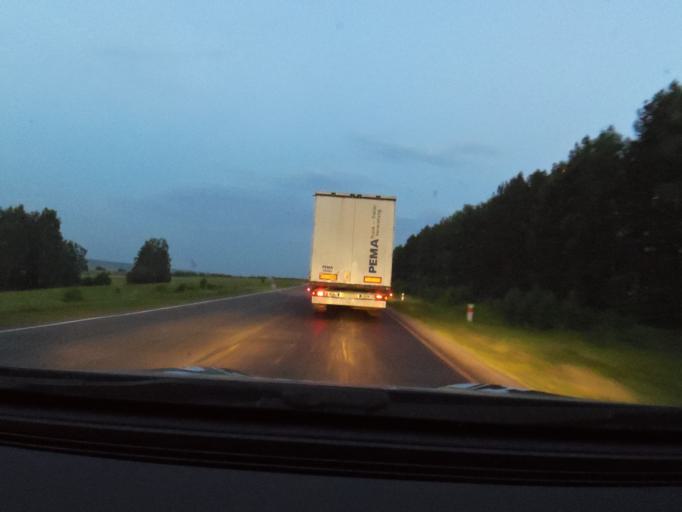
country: RU
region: Bashkortostan
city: Duvan
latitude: 56.0554
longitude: 58.1931
